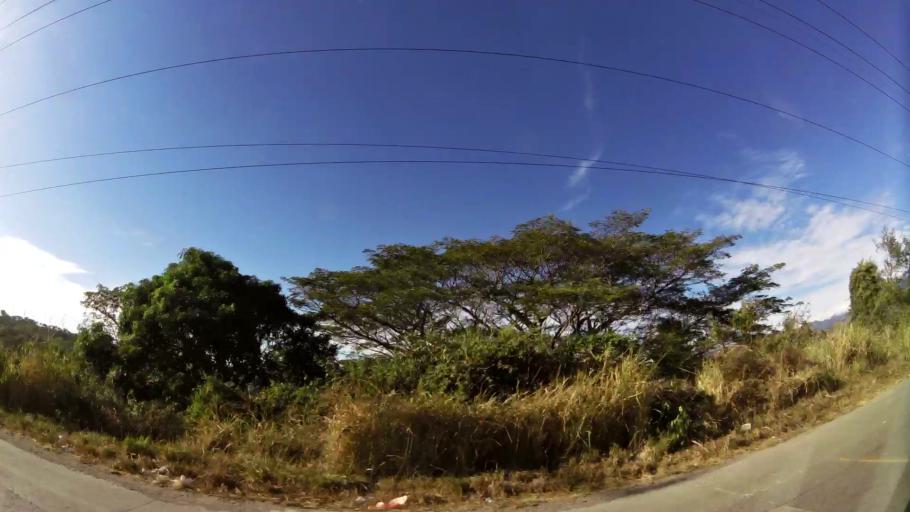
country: SV
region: Santa Ana
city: Metapan
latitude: 14.3015
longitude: -89.4611
